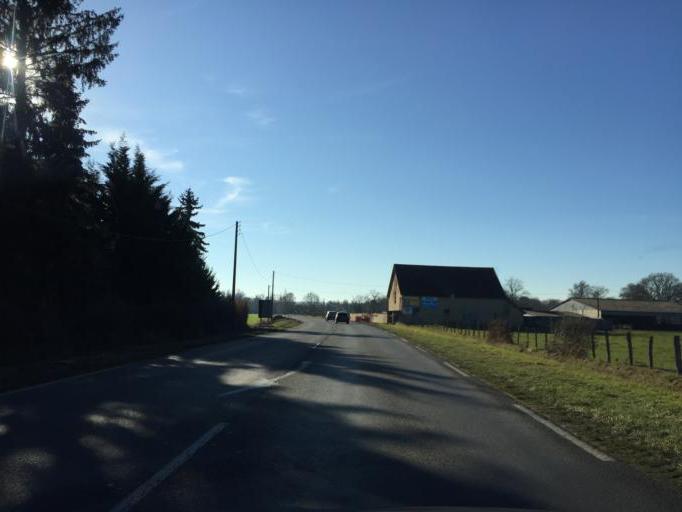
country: FR
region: Auvergne
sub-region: Departement de l'Allier
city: Saint-Remy-en-Rollat
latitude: 46.1688
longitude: 3.3960
